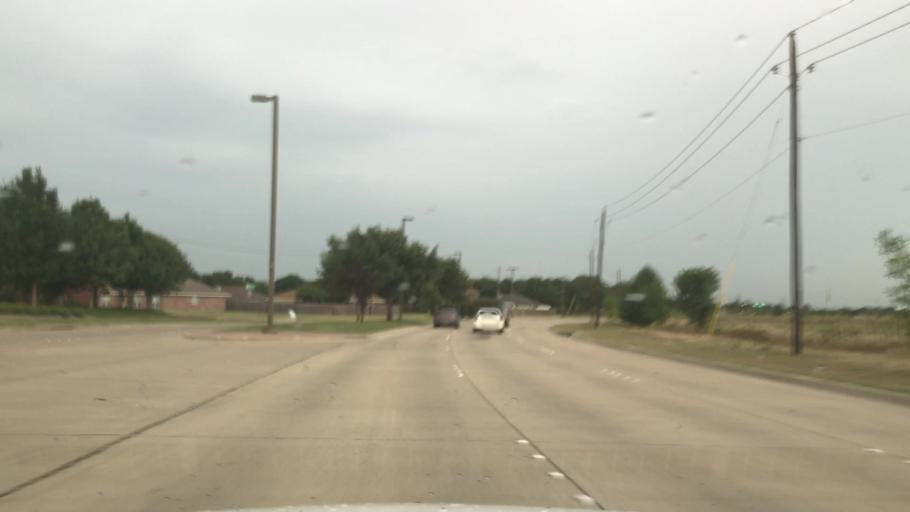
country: US
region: Texas
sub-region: Dallas County
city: Mesquite
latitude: 32.7376
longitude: -96.5632
